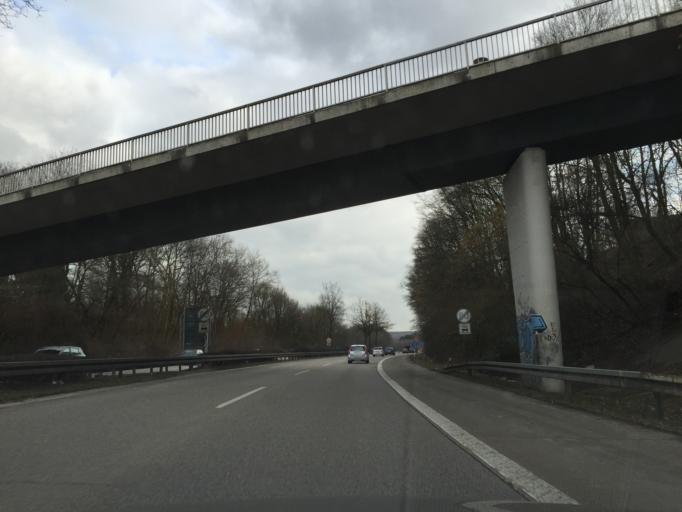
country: DE
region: North Rhine-Westphalia
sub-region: Regierungsbezirk Arnsberg
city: Hagen
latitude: 51.3739
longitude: 7.5034
